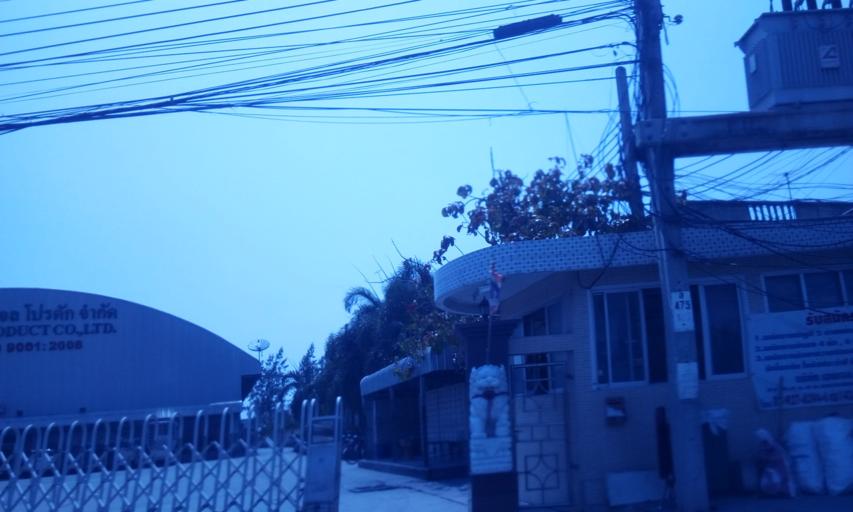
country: TH
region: Nonthaburi
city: Sai Noi
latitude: 13.9238
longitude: 100.3200
